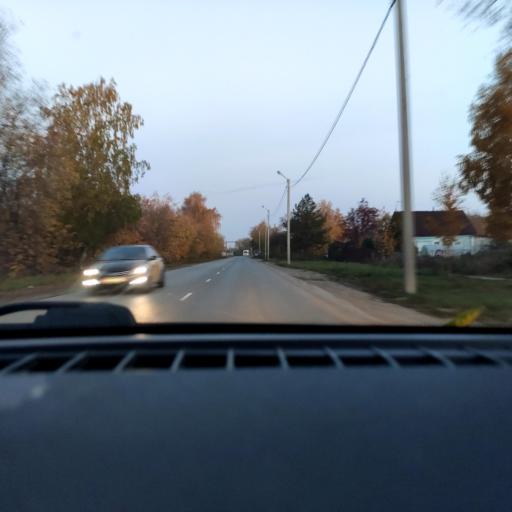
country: RU
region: Perm
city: Kondratovo
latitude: 57.9478
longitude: 56.1431
